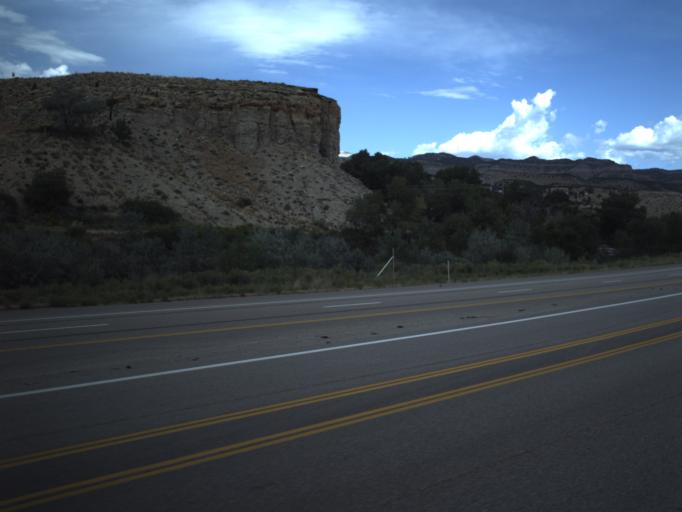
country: US
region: Utah
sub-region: Carbon County
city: Spring Glen
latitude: 39.6409
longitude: -110.8592
